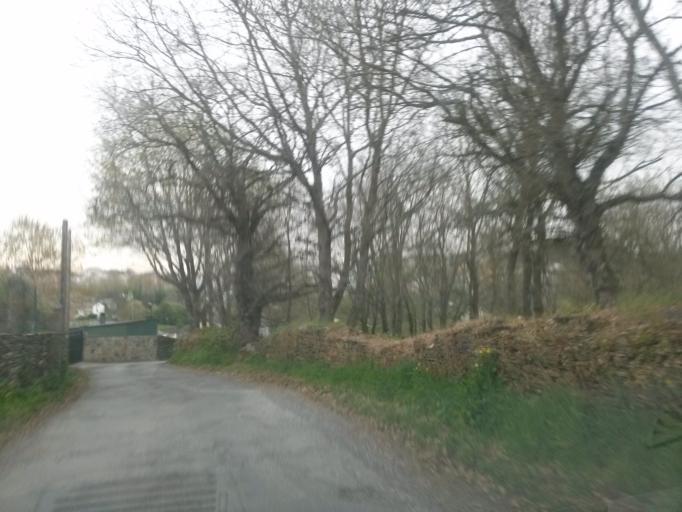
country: ES
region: Galicia
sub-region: Provincia de Lugo
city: Lugo
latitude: 43.0133
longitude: -7.5443
